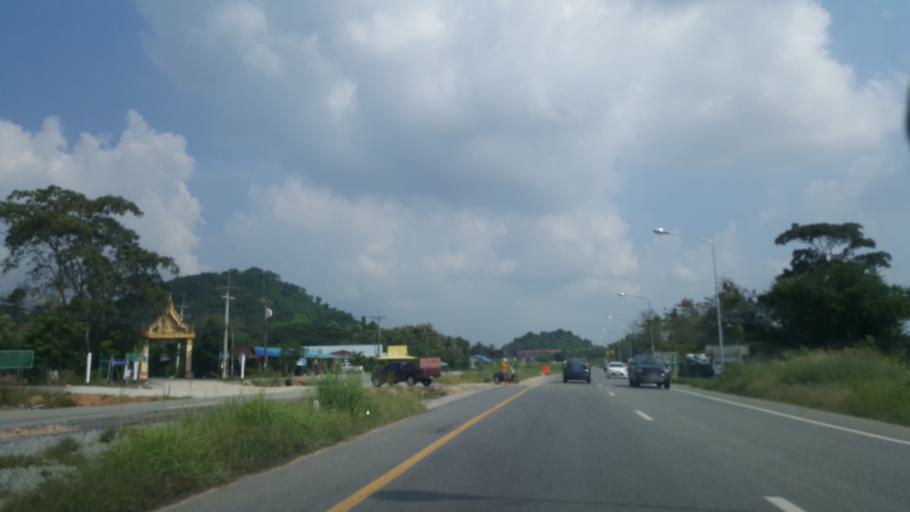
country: TH
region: Rayong
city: Ban Chang
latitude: 12.7351
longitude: 100.9879
